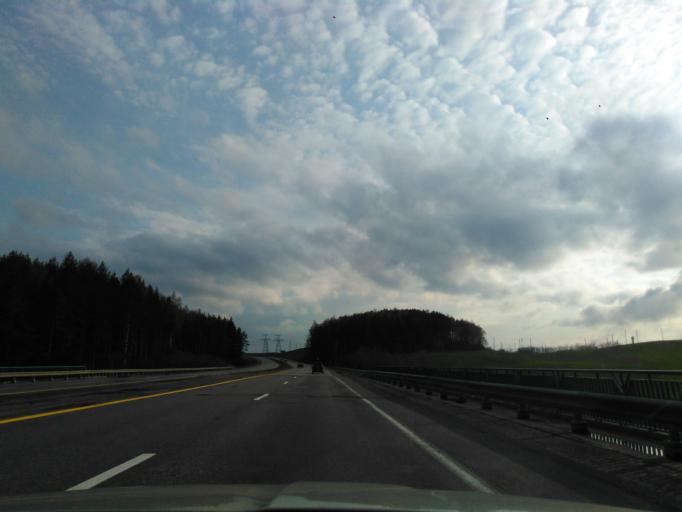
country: BY
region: Minsk
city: Astrashytski Haradok
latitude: 54.0657
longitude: 27.7154
